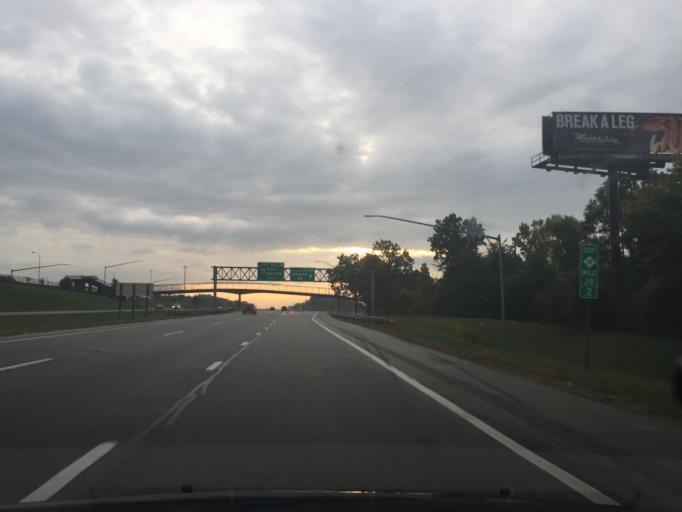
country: US
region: Michigan
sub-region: Oakland County
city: Pontiac
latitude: 42.6420
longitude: -83.2576
